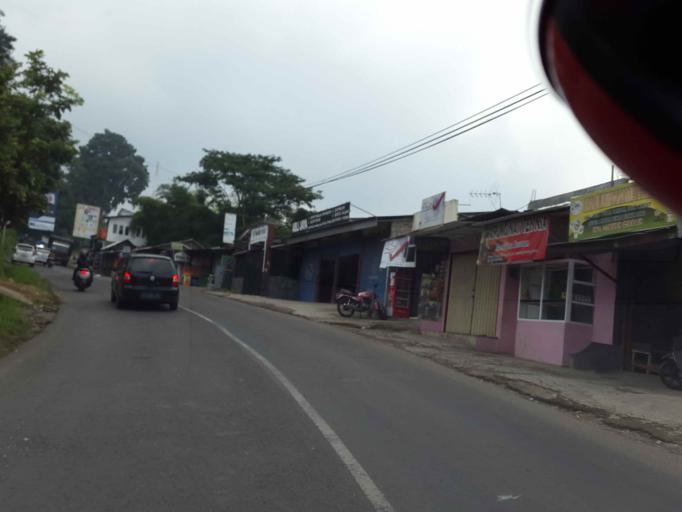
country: ID
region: West Java
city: Lembang
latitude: -6.8305
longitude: 107.6069
